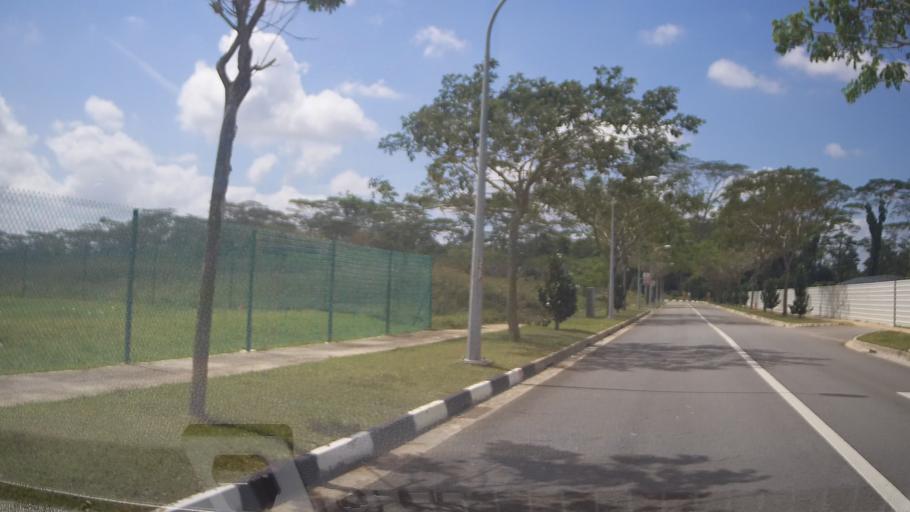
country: MY
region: Johor
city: Johor Bahru
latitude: 1.4203
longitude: 103.7221
